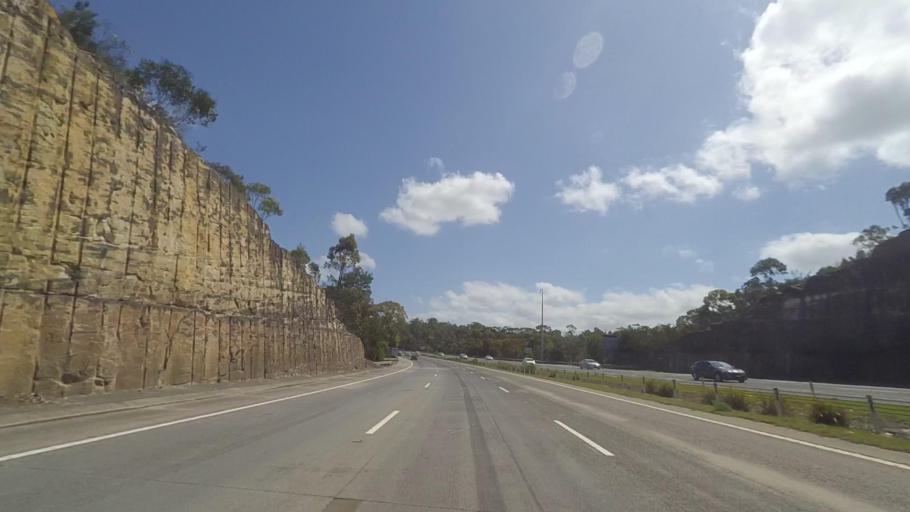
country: AU
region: New South Wales
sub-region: Hornsby Shire
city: Berowra
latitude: -33.6446
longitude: 151.1399
